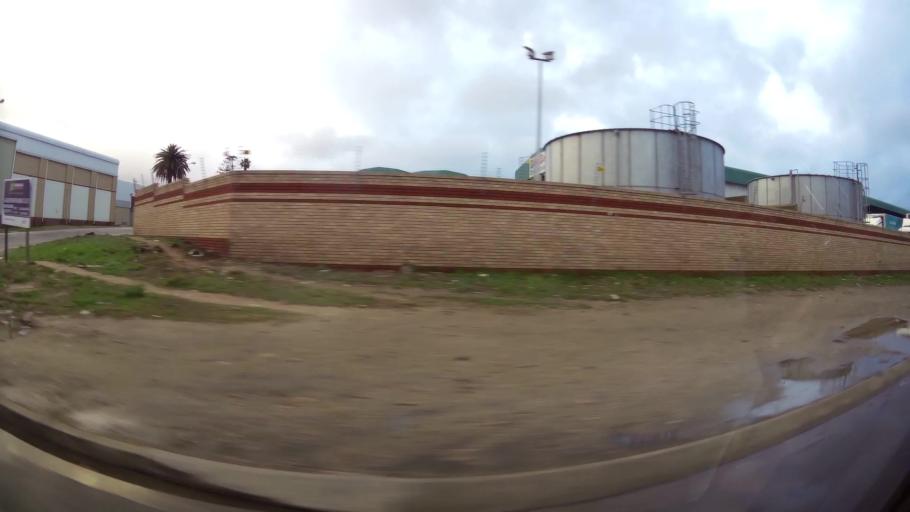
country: ZA
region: Eastern Cape
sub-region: Nelson Mandela Bay Metropolitan Municipality
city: Port Elizabeth
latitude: -33.9290
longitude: 25.6045
